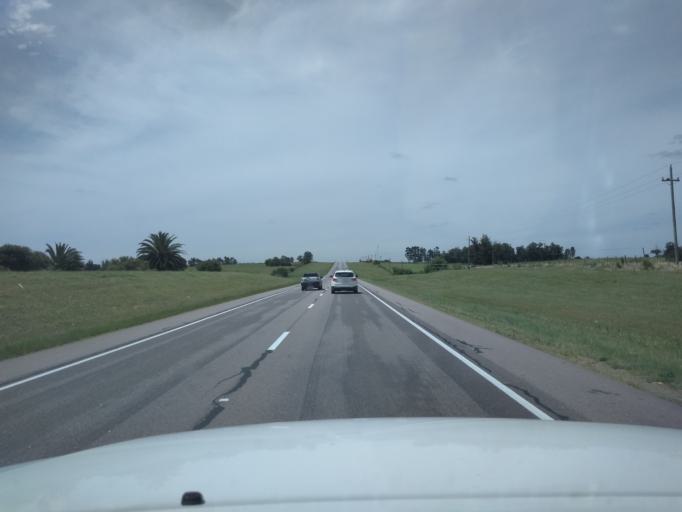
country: UY
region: Florida
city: Florida
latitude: -34.2188
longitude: -56.2083
